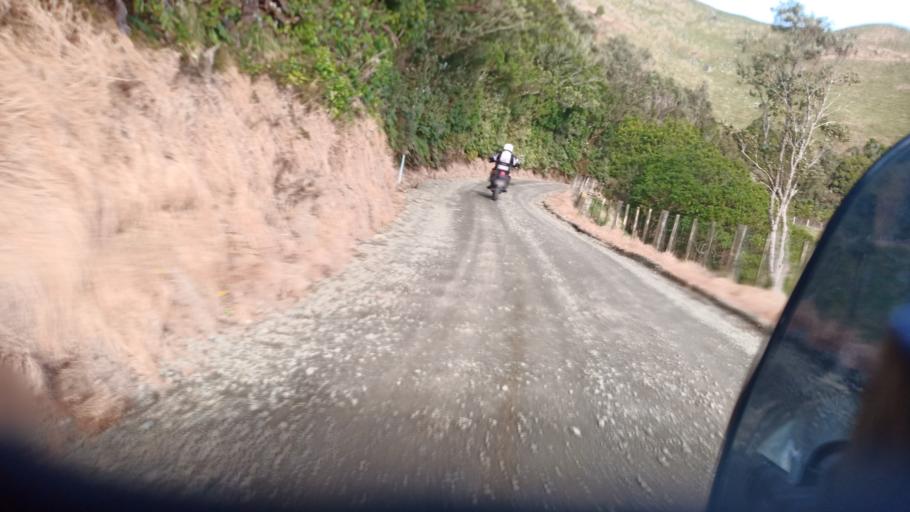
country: NZ
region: Gisborne
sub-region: Gisborne District
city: Gisborne
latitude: -38.4627
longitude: 177.5363
